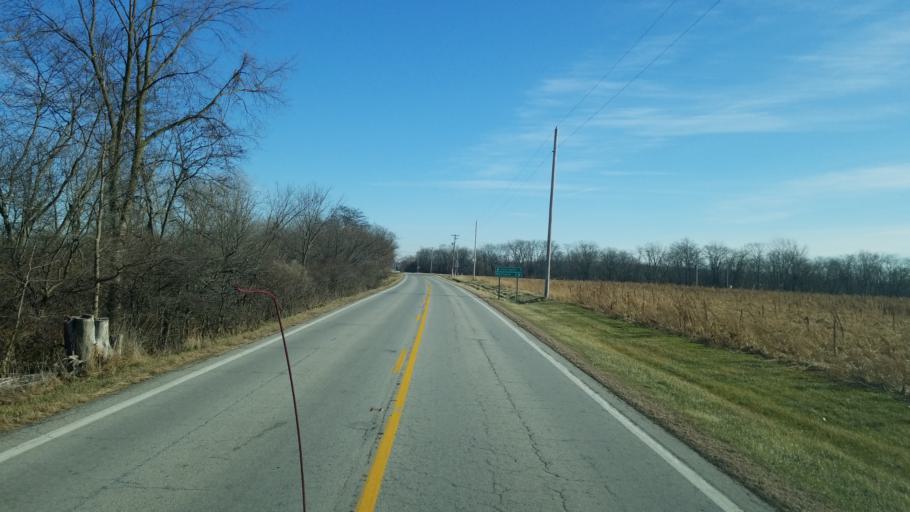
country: US
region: Ohio
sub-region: Henry County
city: Liberty Center
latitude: 41.4151
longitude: -83.9440
